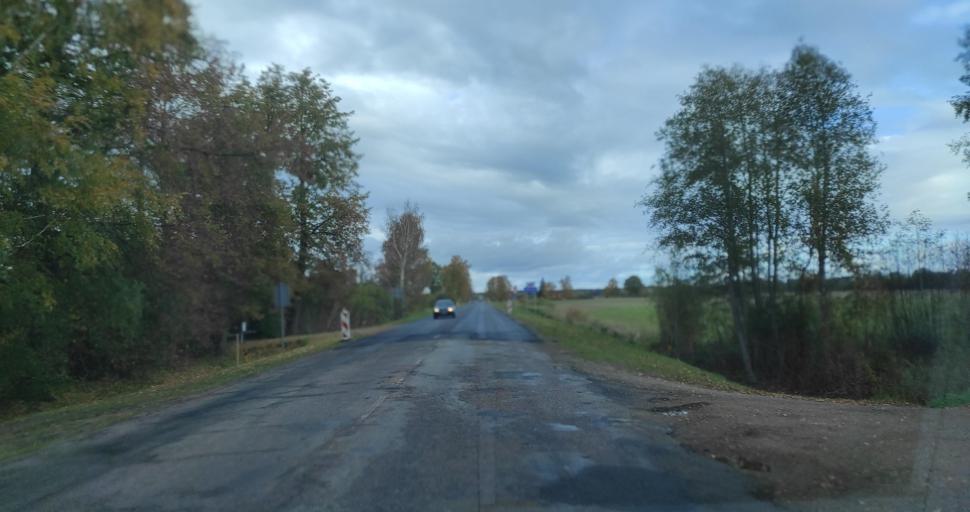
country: LV
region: Skrunda
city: Skrunda
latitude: 56.6852
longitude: 22.0177
